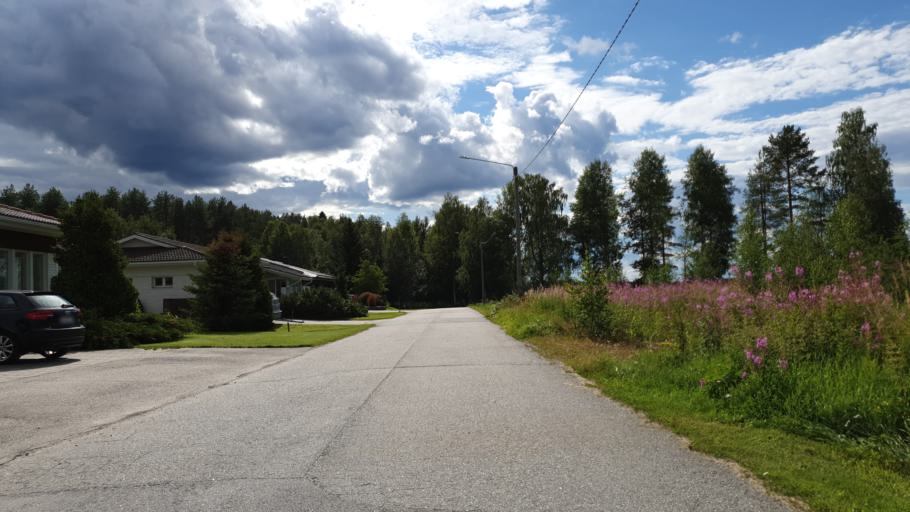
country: FI
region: Kainuu
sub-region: Kehys-Kainuu
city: Kuhmo
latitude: 64.1336
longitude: 29.5277
